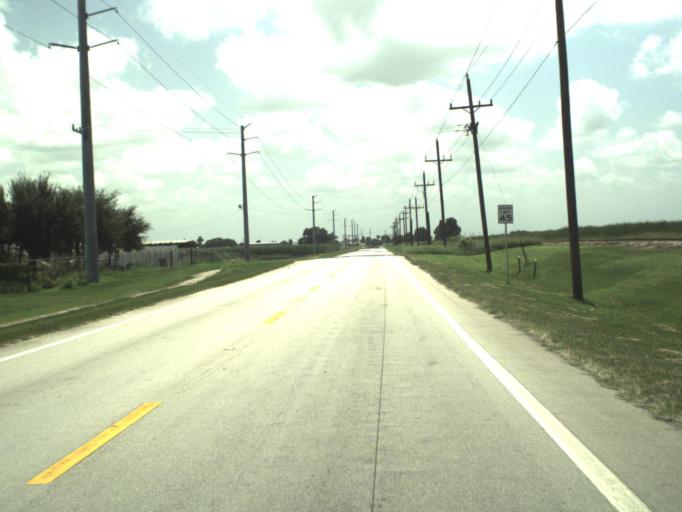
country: US
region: Florida
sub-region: Palm Beach County
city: Pahokee
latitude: 26.8409
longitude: -80.6445
